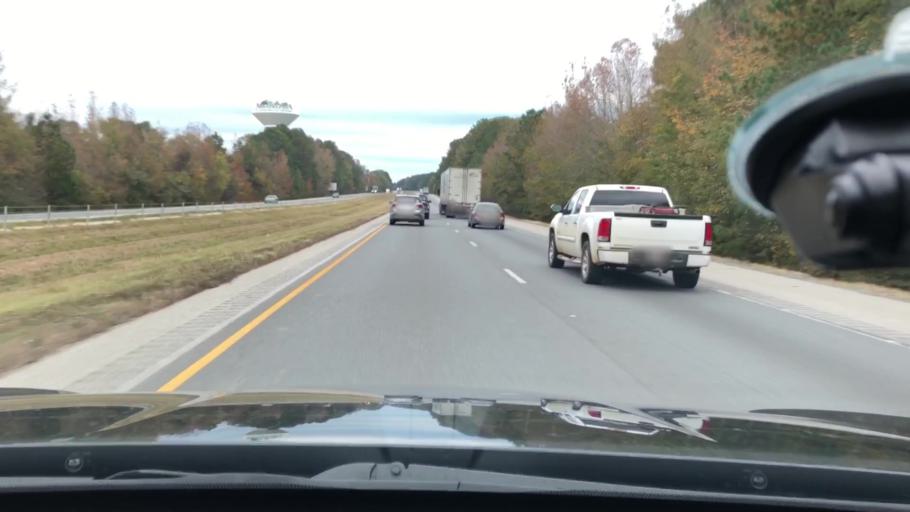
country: US
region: Arkansas
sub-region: Clark County
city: Arkadelphia
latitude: 34.1300
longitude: -93.0866
